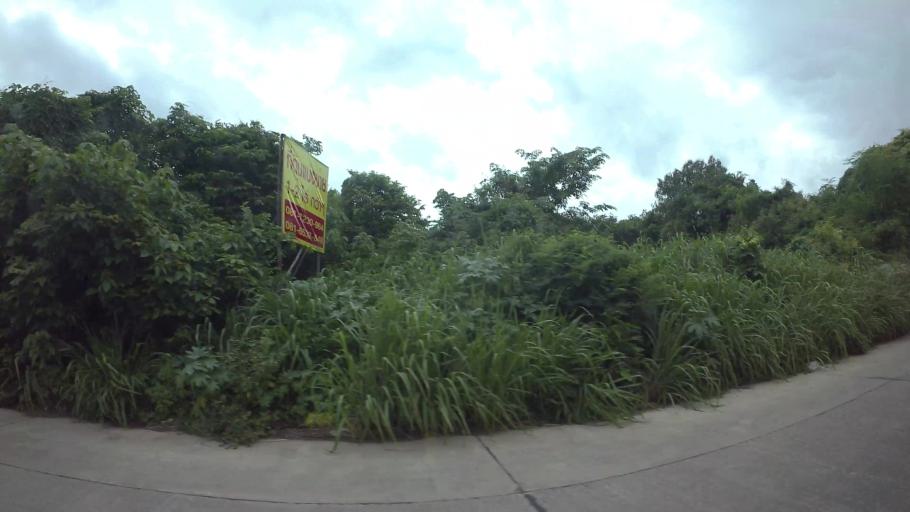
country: TH
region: Chon Buri
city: Si Racha
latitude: 13.2063
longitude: 100.9472
